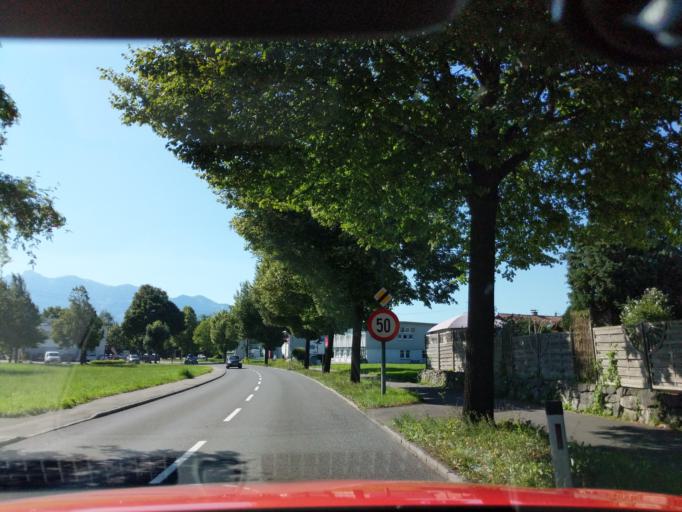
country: AT
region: Vorarlberg
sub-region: Politischer Bezirk Feldkirch
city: Rankweil
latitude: 47.2723
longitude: 9.6254
